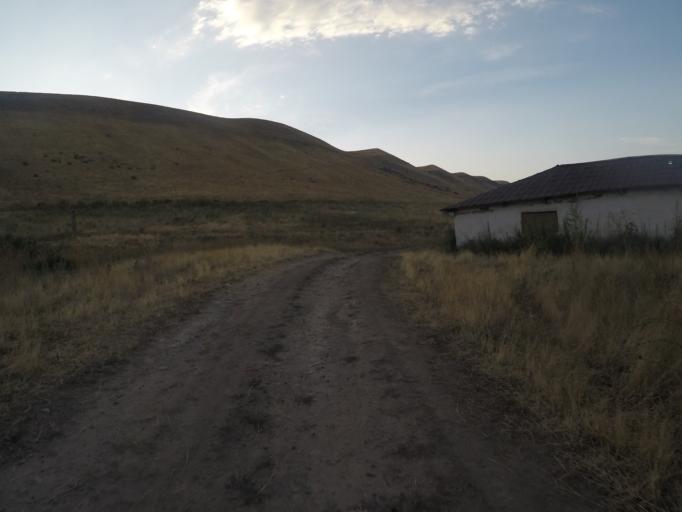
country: KG
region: Chuy
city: Bishkek
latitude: 42.7654
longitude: 74.6381
